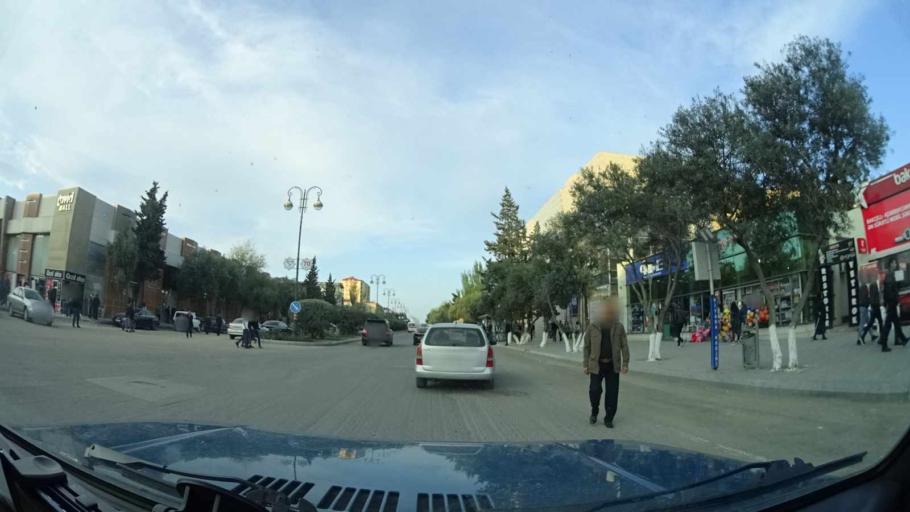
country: AZ
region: Sumqayit
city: Sumqayit
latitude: 40.5884
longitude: 49.6737
